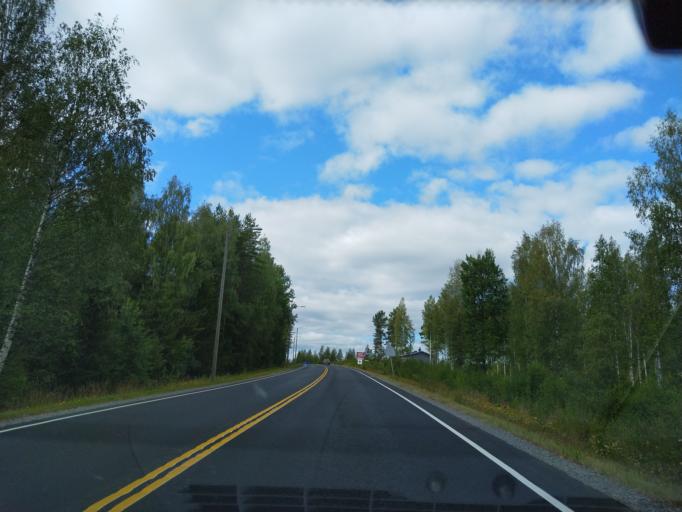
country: FI
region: Haeme
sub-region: Riihimaeki
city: Loppi
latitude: 60.7205
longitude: 24.4556
